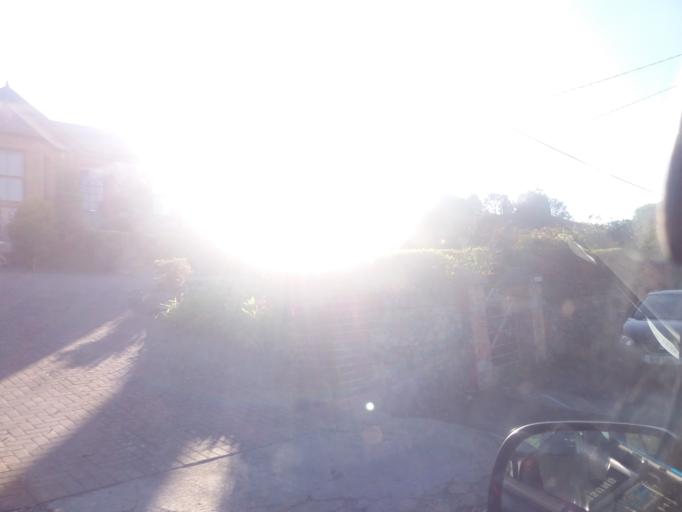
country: IE
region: Leinster
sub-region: Fingal County
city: Howth
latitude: 53.3758
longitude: -6.0621
